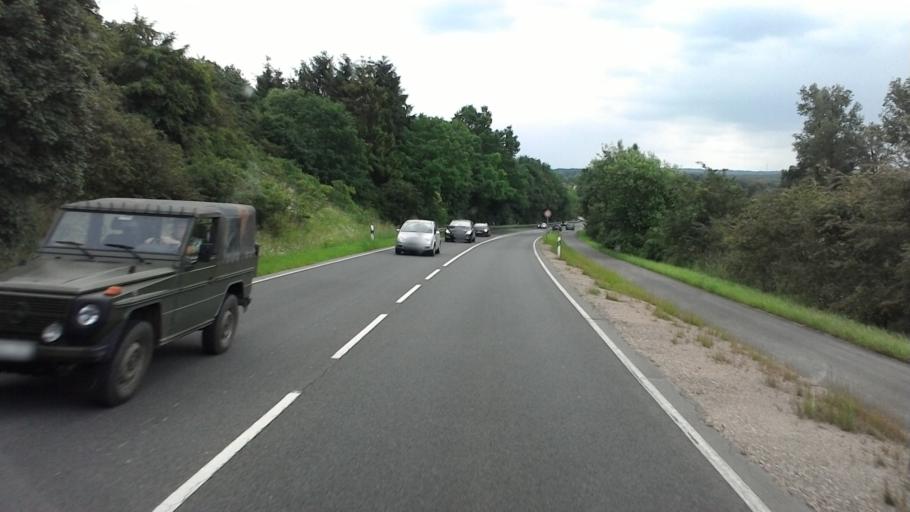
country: BE
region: Wallonia
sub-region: Province de Liege
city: Raeren
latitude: 50.7025
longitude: 6.1515
